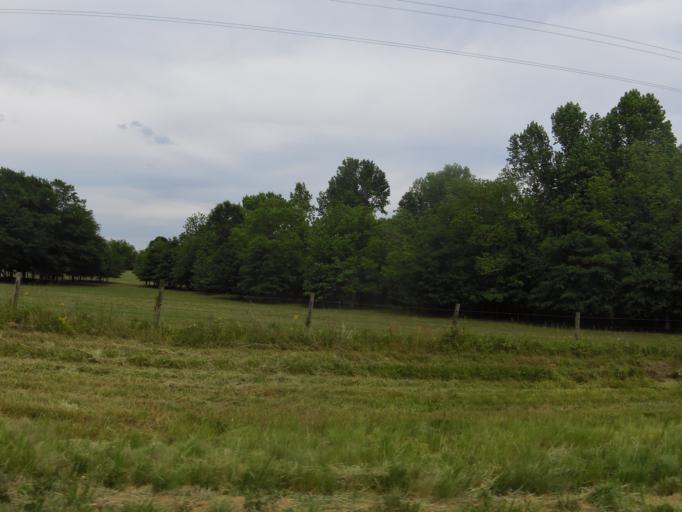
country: US
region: Georgia
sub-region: McDuffie County
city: Thomson
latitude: 33.3850
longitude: -82.4725
